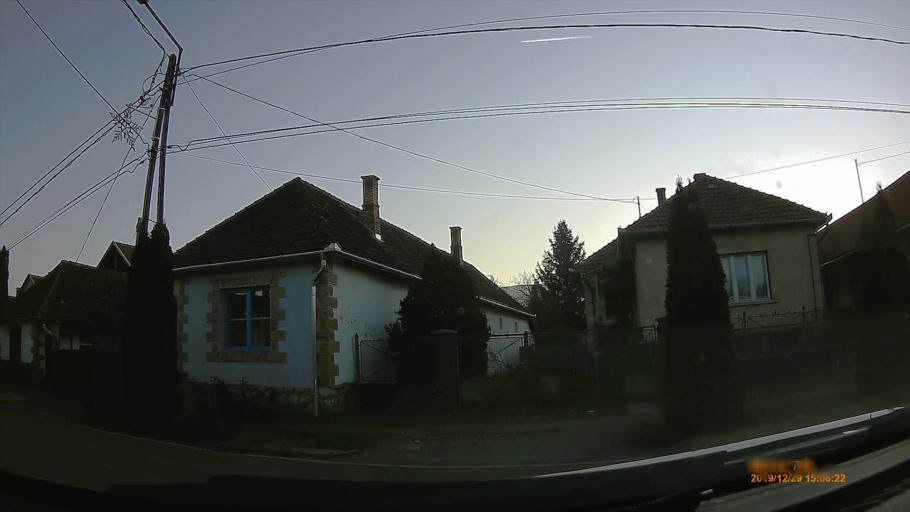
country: HU
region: Heves
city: Parad
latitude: 47.9241
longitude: 20.0266
